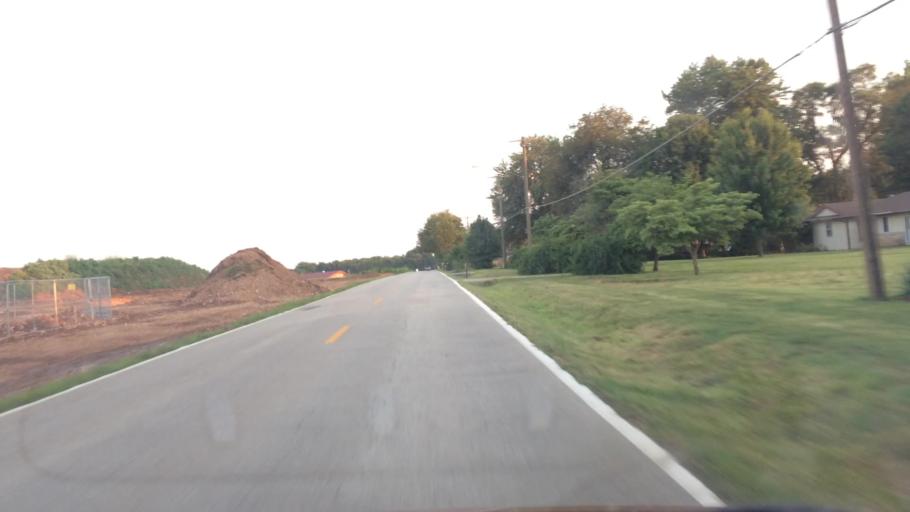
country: US
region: Missouri
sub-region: Greene County
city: Springfield
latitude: 37.2034
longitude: -93.3742
